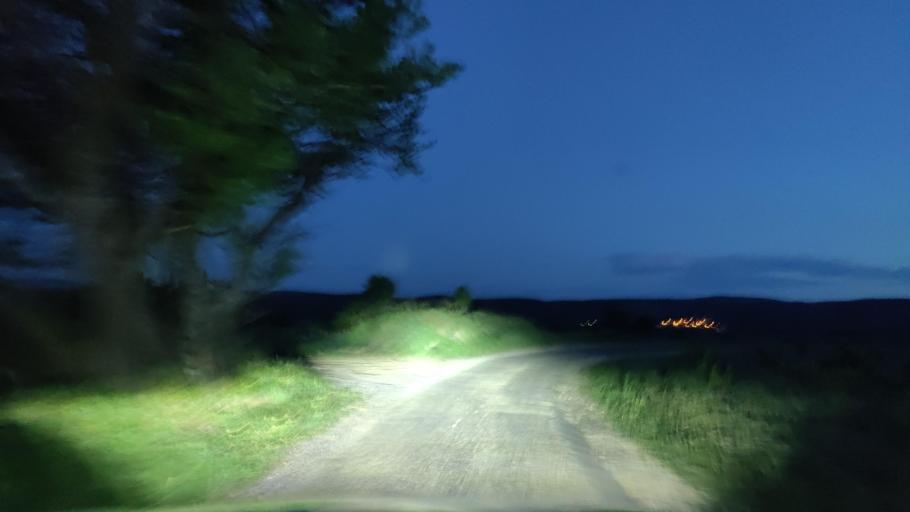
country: FR
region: Languedoc-Roussillon
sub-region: Departement des Pyrenees-Orientales
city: Estagel
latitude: 42.8739
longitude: 2.7302
